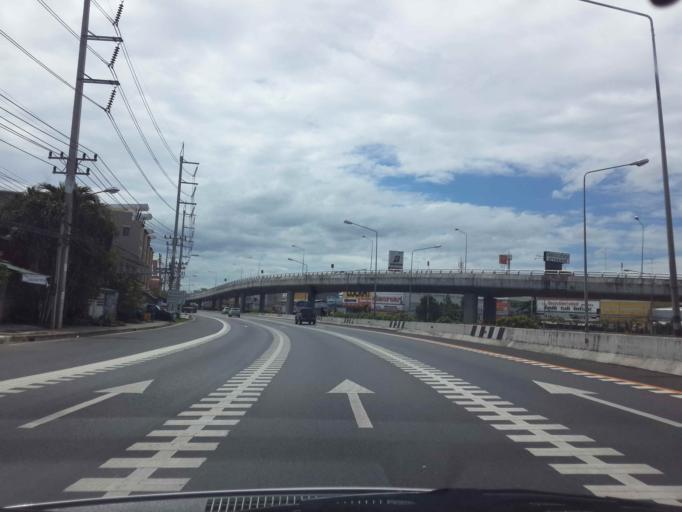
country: TH
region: Phetchaburi
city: Phetchaburi
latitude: 13.1125
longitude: 99.9309
